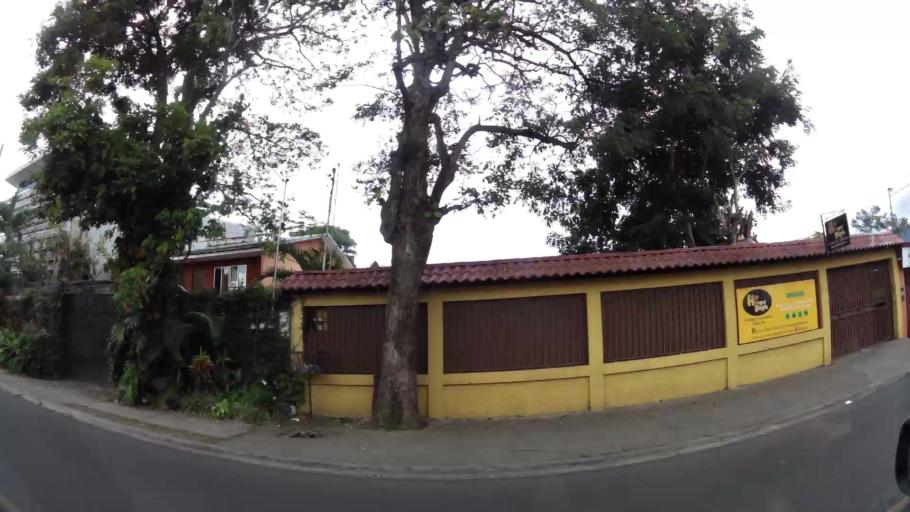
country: CR
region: San Jose
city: Santa Ana
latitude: 9.9521
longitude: -84.1897
